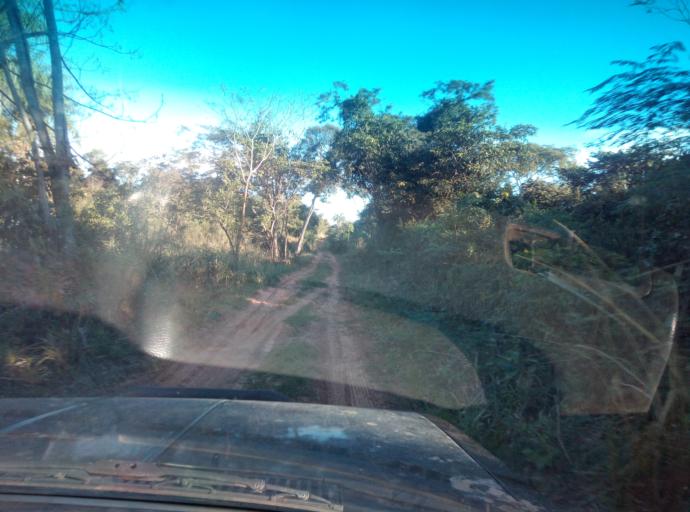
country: PY
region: Caaguazu
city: Carayao
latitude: -25.1835
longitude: -56.2624
